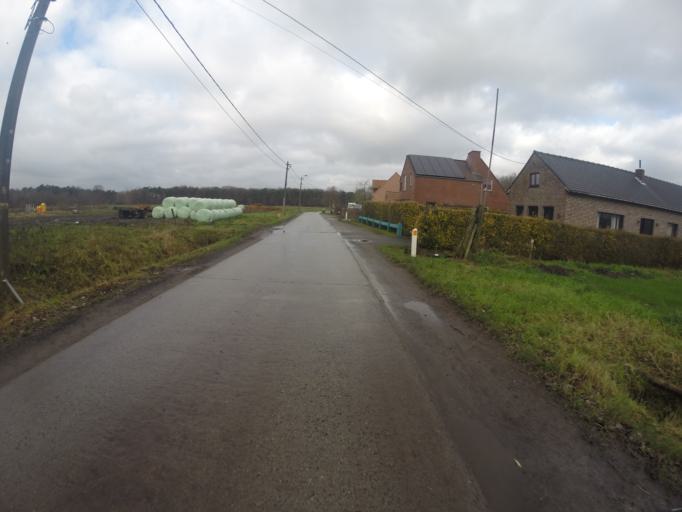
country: BE
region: Flanders
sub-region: Provincie Oost-Vlaanderen
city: Zomergem
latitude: 51.1399
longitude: 3.5232
